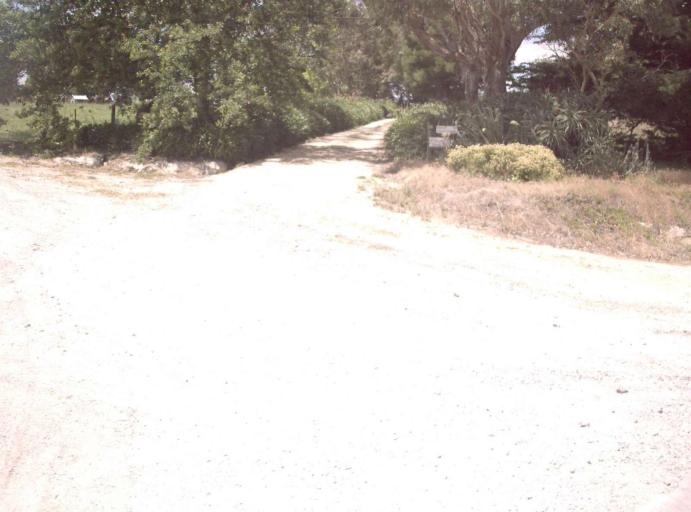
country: AU
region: Victoria
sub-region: Bass Coast
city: North Wonthaggi
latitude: -38.5997
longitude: 146.0193
